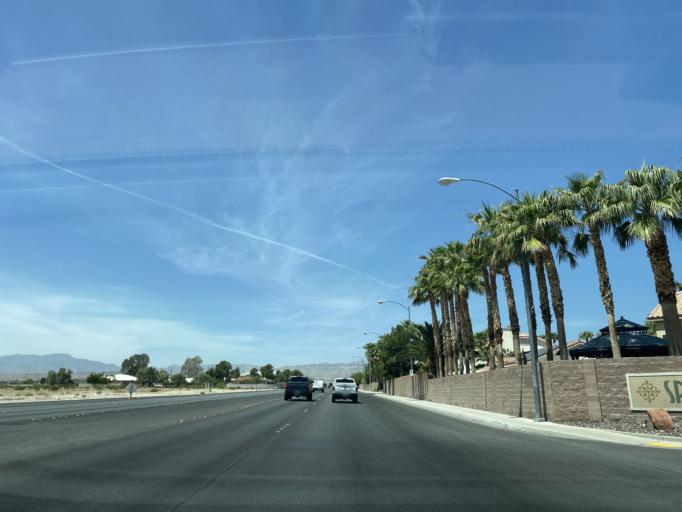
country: US
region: Nevada
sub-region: Clark County
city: Spring Valley
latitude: 36.0854
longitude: -115.2295
